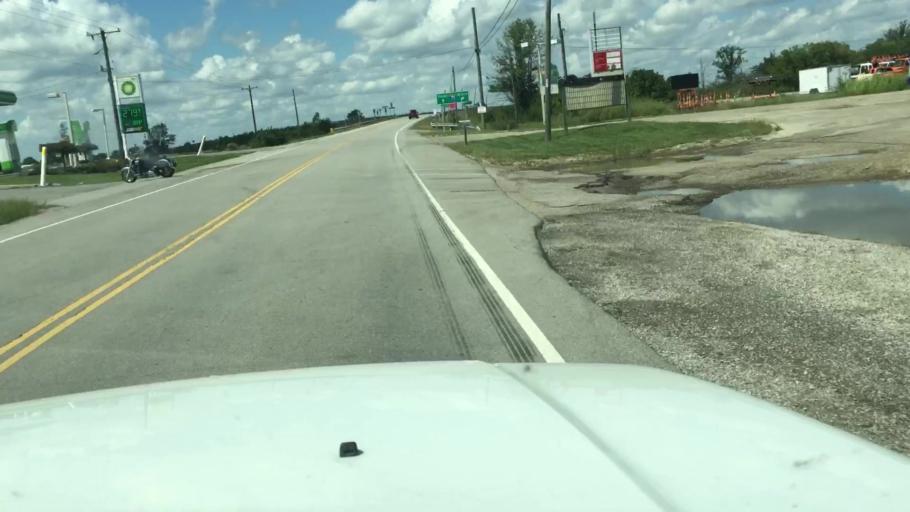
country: US
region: Ohio
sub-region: Madison County
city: Mount Sterling
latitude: 39.7555
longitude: -83.2995
